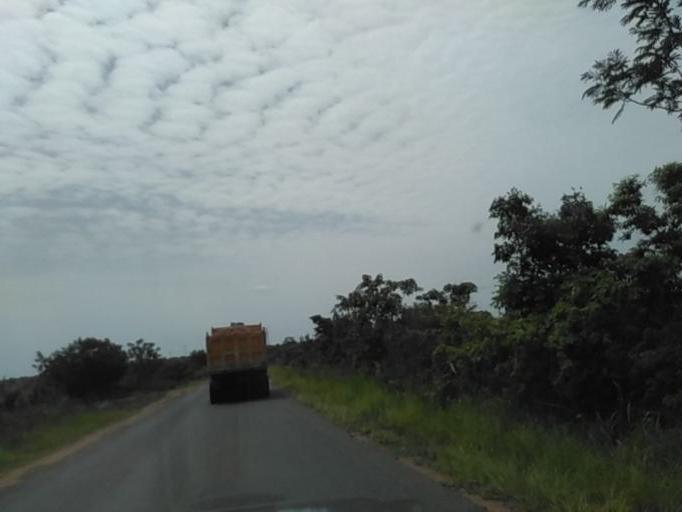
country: GH
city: Akropong
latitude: 6.0956
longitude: 0.0563
